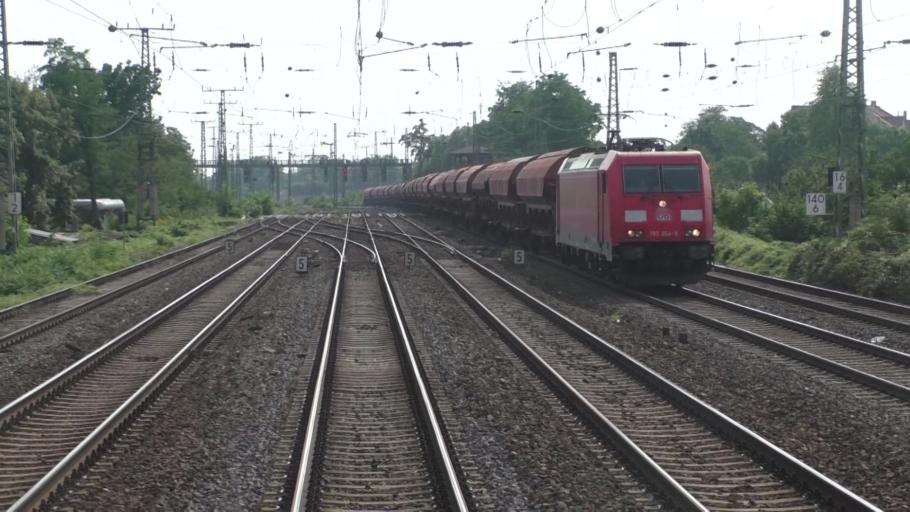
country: DE
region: Saxony-Anhalt
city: Neue Neustadt
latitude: 52.1417
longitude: 11.6329
